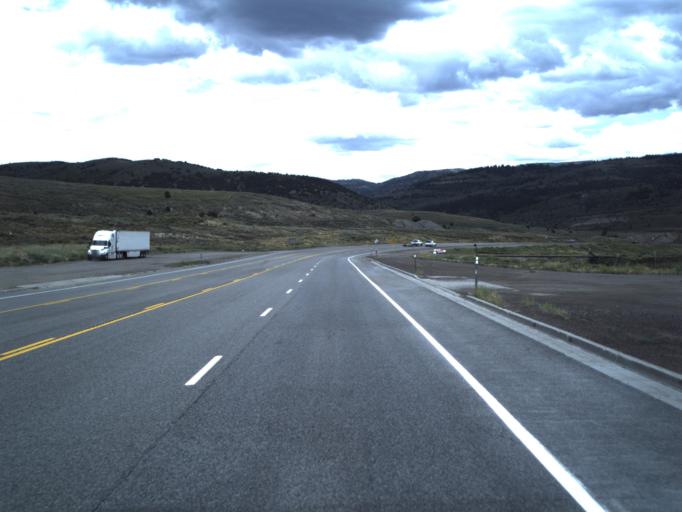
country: US
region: Utah
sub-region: Carbon County
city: Helper
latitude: 39.9284
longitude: -111.0790
